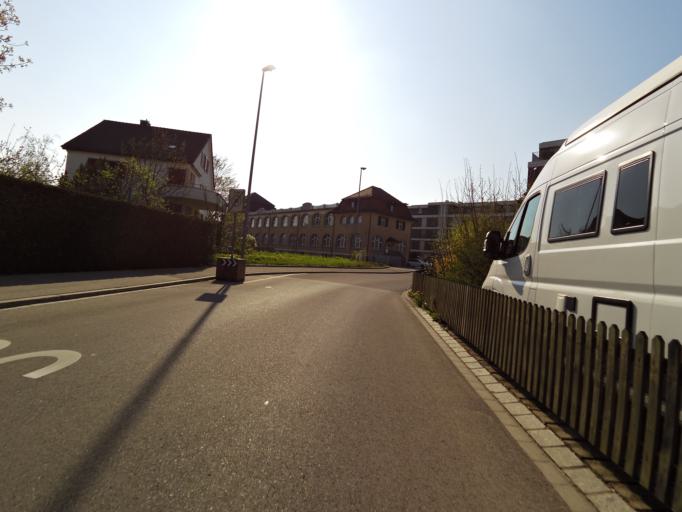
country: CH
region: Thurgau
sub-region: Frauenfeld District
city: Frauenfeld
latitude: 47.5569
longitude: 8.8884
